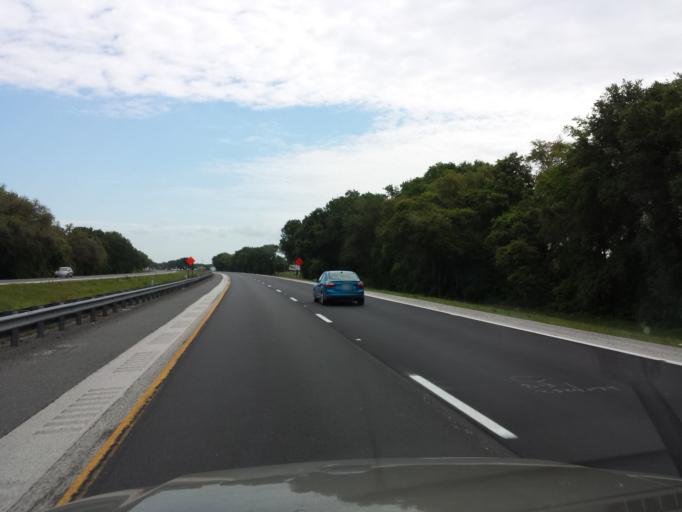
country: US
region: Florida
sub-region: Sumter County
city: Bushnell
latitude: 28.6318
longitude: -82.1690
